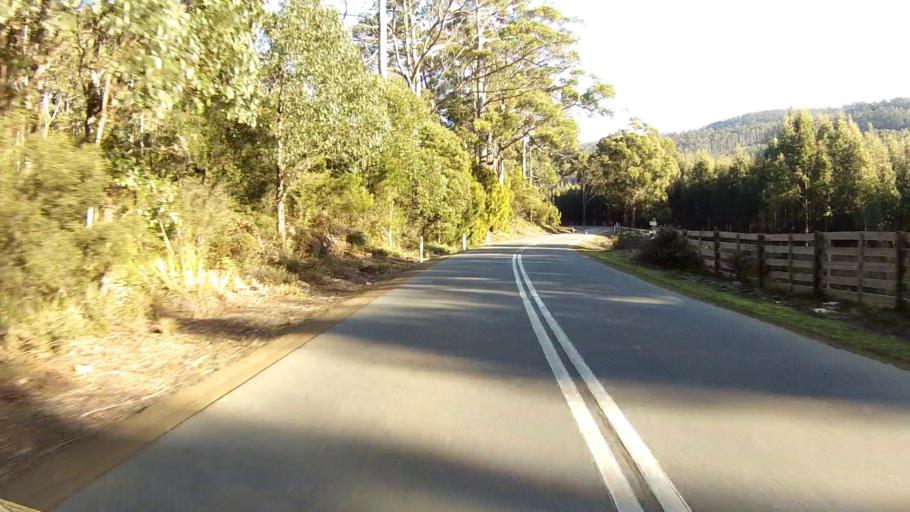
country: AU
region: Tasmania
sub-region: Clarence
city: Sandford
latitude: -43.1003
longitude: 147.8669
